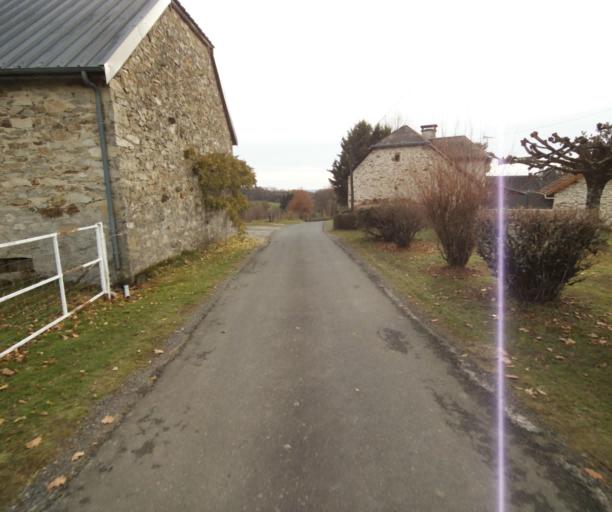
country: FR
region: Limousin
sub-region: Departement de la Correze
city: Saint-Mexant
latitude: 45.2620
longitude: 1.6468
